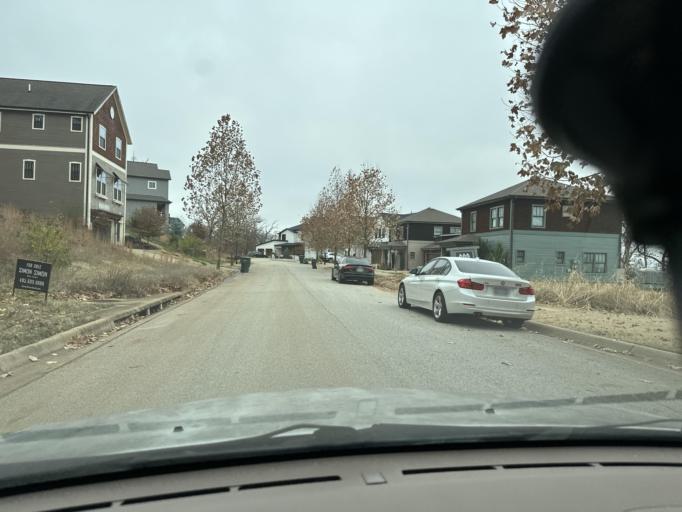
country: US
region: Arkansas
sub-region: Washington County
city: Fayetteville
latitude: 36.0934
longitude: -94.1506
